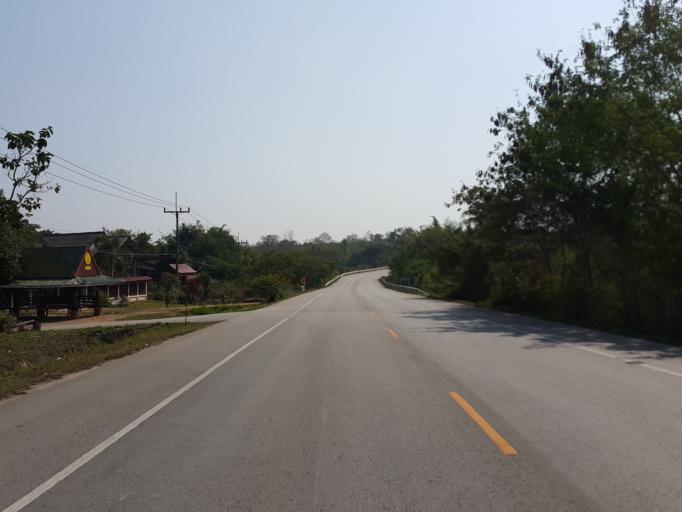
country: TH
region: Lampang
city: Wang Nuea
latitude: 18.9646
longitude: 99.6123
